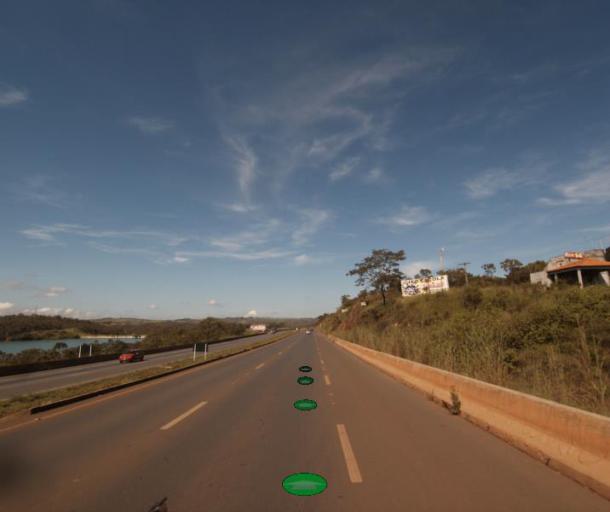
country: BR
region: Federal District
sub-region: Brasilia
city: Brasilia
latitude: -15.7733
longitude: -48.2316
